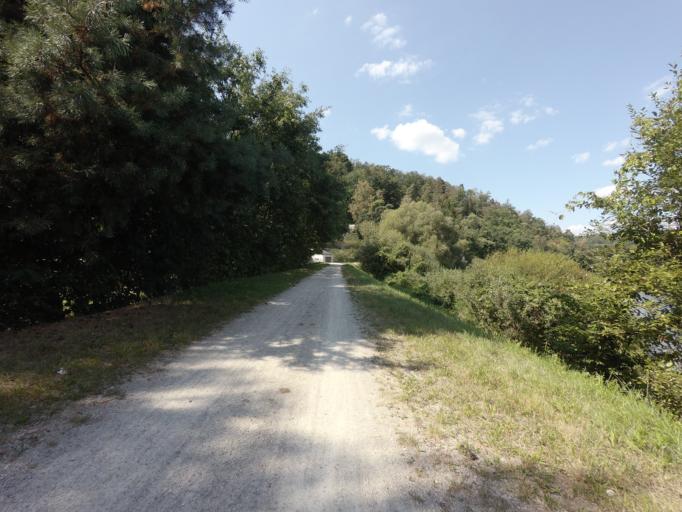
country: CZ
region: Jihocesky
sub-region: Okres Ceske Budejovice
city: Hluboka nad Vltavou
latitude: 49.0572
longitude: 14.4425
